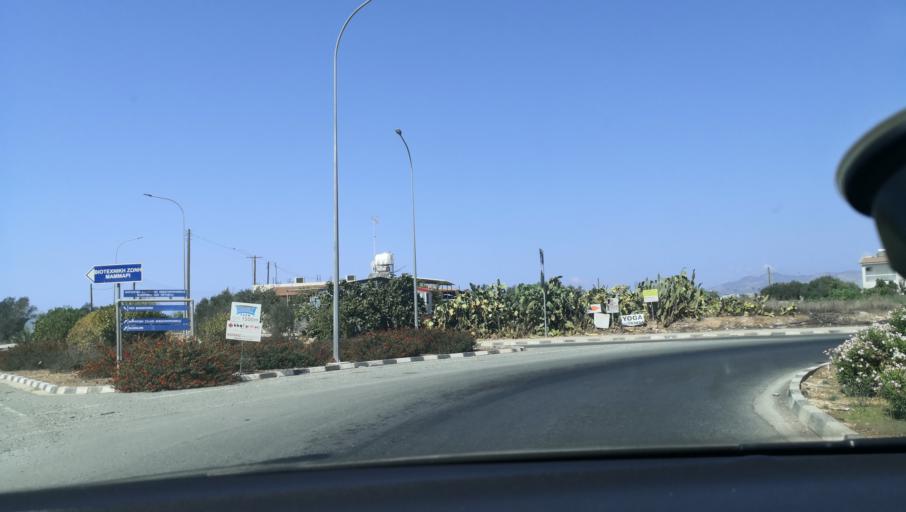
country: CY
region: Lefkosia
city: Kokkinotrimithia
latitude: 35.1574
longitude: 33.1982
